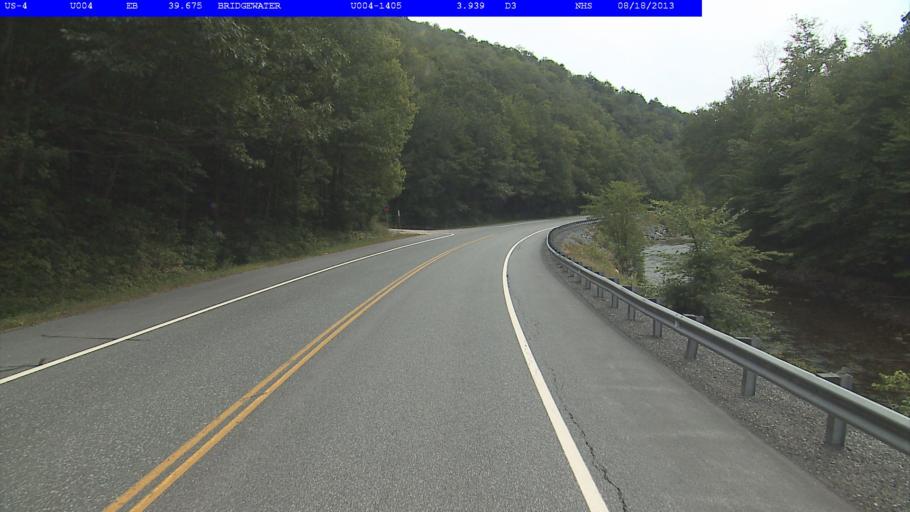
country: US
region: Vermont
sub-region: Windsor County
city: Woodstock
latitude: 43.5981
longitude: -72.6837
